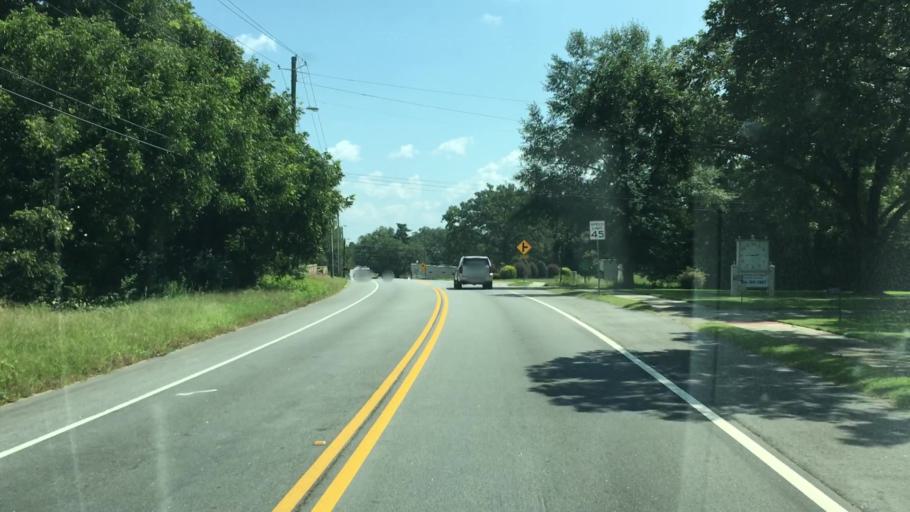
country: US
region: Georgia
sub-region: Oconee County
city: Watkinsville
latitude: 33.8218
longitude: -83.4404
